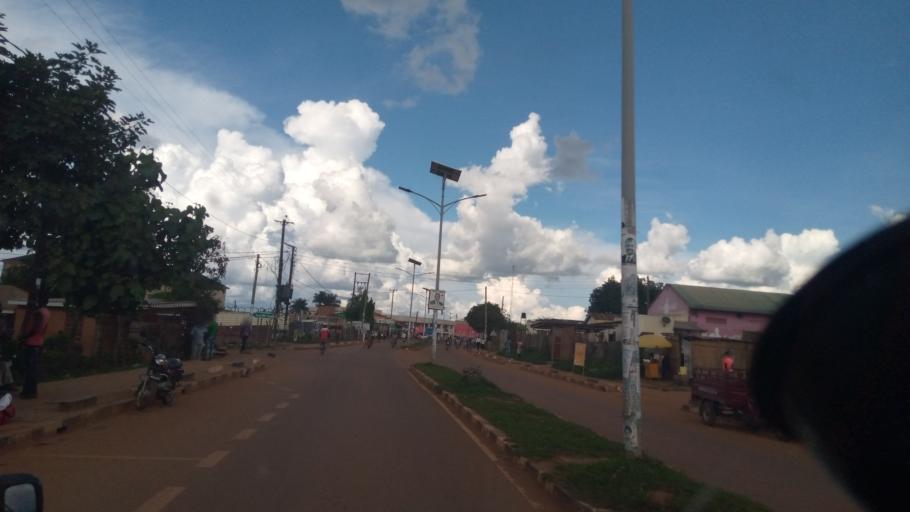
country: UG
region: Northern Region
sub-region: Lira District
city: Lira
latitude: 2.2422
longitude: 32.8921
